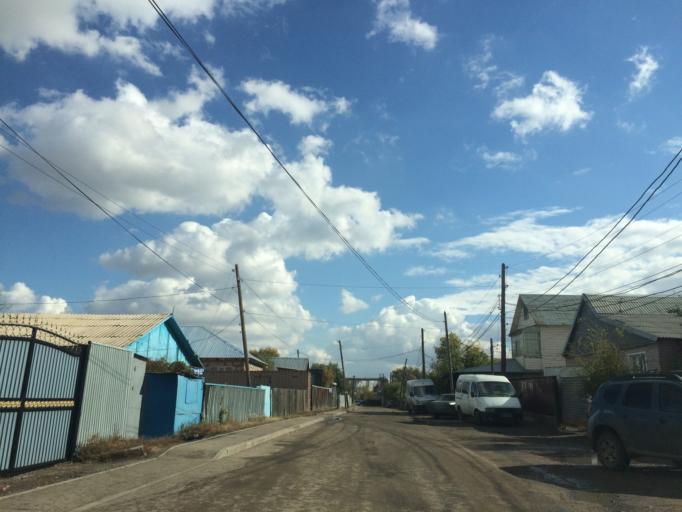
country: KZ
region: Astana Qalasy
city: Astana
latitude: 51.1860
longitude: 71.3865
